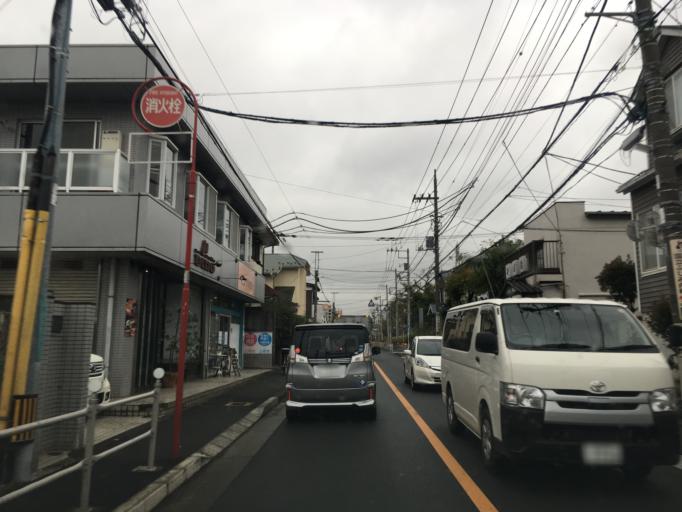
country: JP
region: Tokyo
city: Kokubunji
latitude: 35.6904
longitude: 139.4413
